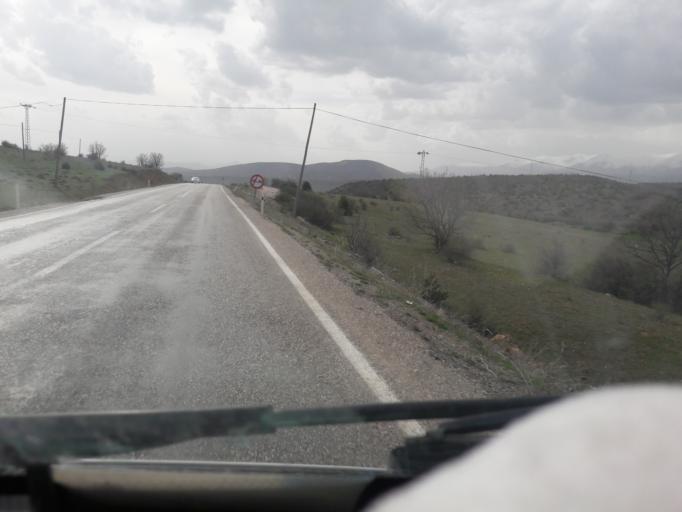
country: TR
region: Gumushane
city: Evren
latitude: 40.1710
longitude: 39.2454
